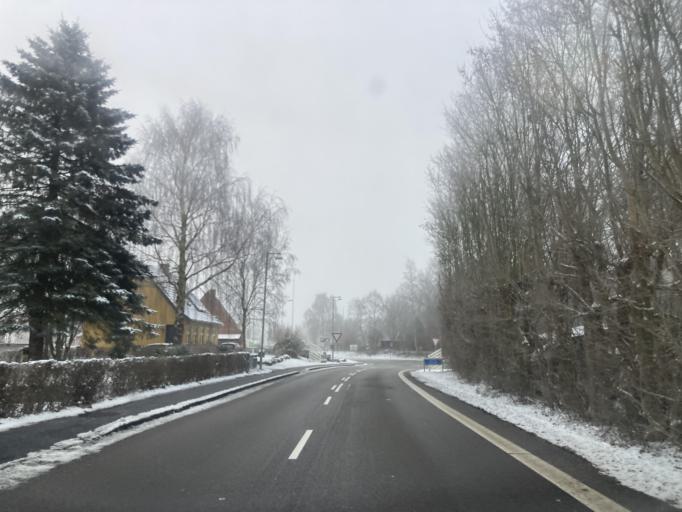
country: DK
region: Zealand
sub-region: Soro Kommune
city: Stenlille
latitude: 55.5432
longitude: 11.6039
